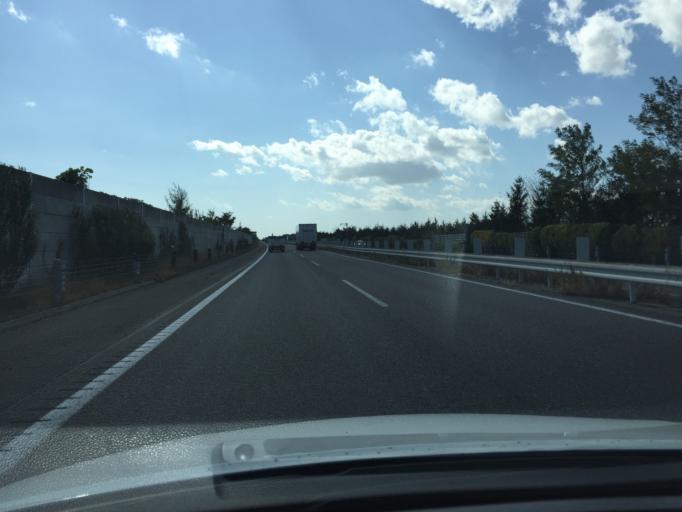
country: JP
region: Fukushima
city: Koriyama
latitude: 37.4518
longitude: 140.3538
